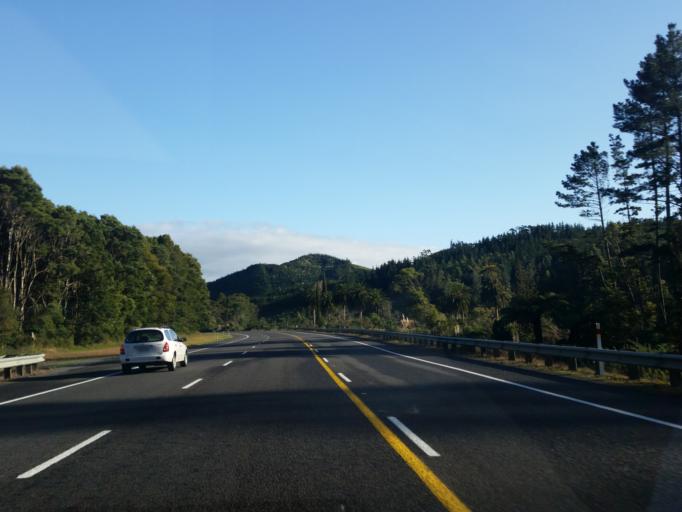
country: NZ
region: Bay of Plenty
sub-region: Western Bay of Plenty District
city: Waihi Beach
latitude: -37.4600
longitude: 175.9094
